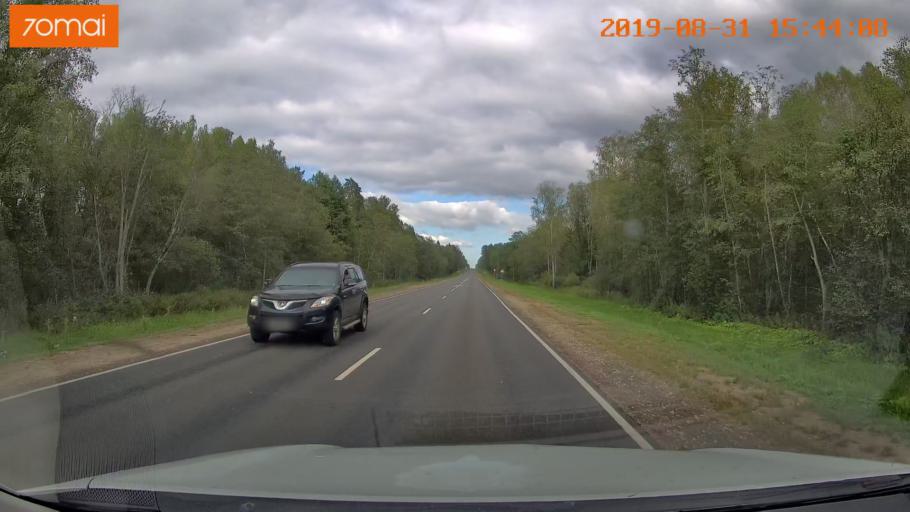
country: RU
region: Kaluga
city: Mosal'sk
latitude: 54.6570
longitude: 34.9254
